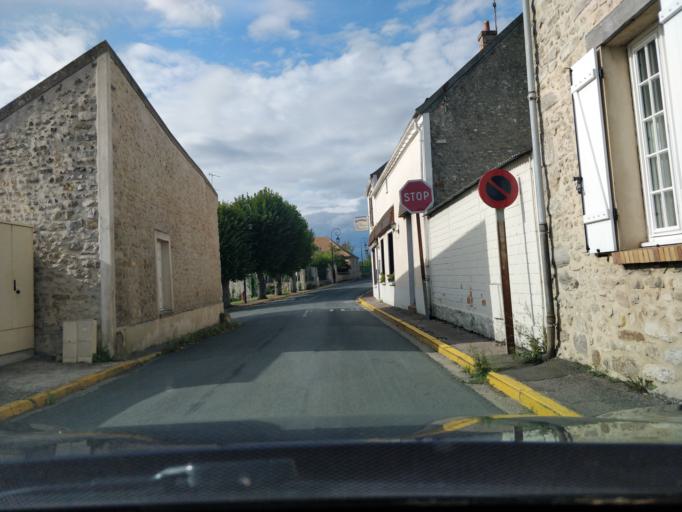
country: FR
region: Ile-de-France
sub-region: Departement de l'Essonne
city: Etampes
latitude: 48.4034
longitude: 2.1499
